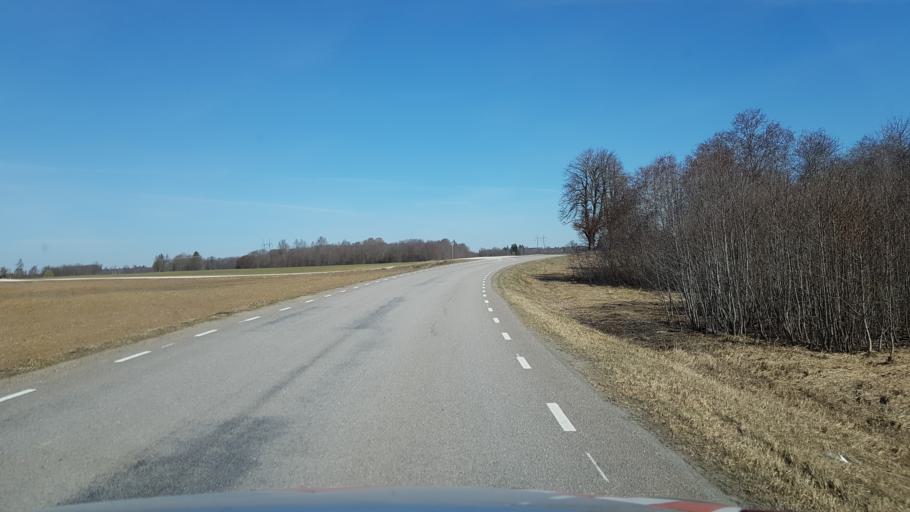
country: EE
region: Laeaene-Virumaa
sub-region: Vinni vald
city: Vinni
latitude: 59.2359
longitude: 26.3426
